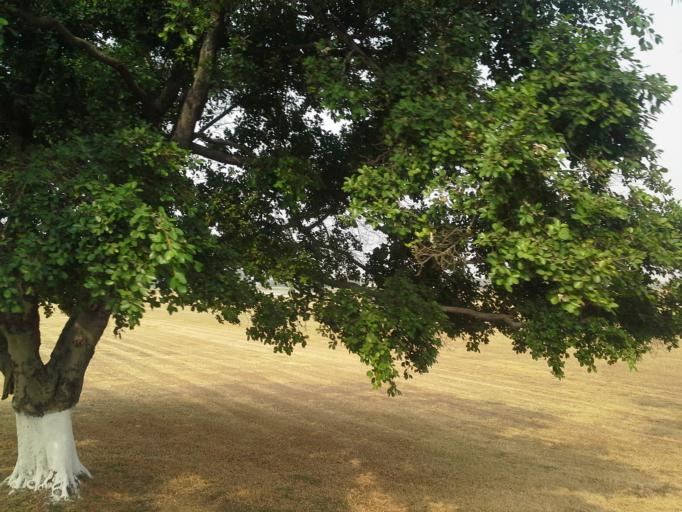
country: IN
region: Telangana
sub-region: Medak
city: Patancheru
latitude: 17.5139
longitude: 78.2752
